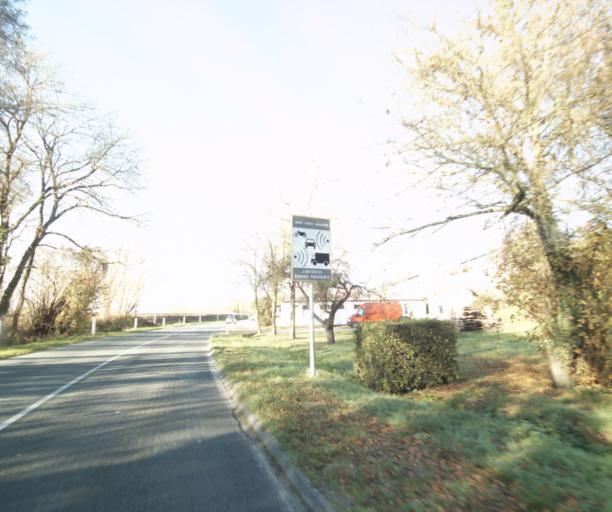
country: FR
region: Poitou-Charentes
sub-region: Departement de la Charente-Maritime
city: Chaniers
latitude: 45.7274
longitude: -0.5836
